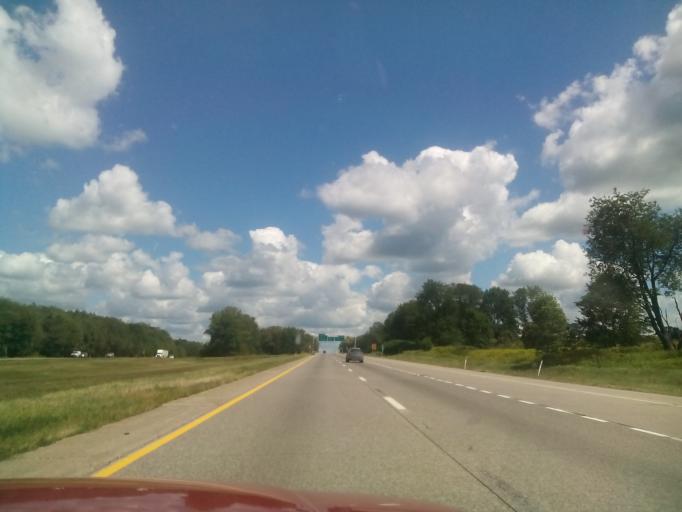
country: US
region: Pennsylvania
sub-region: Luzerne County
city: Conyngham
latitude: 41.0435
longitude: -76.0238
